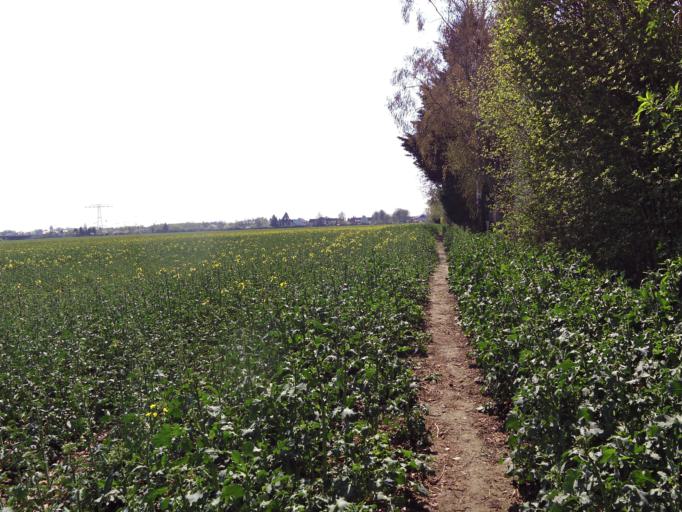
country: DE
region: Saxony
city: Leipzig
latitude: 51.3860
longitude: 12.3342
